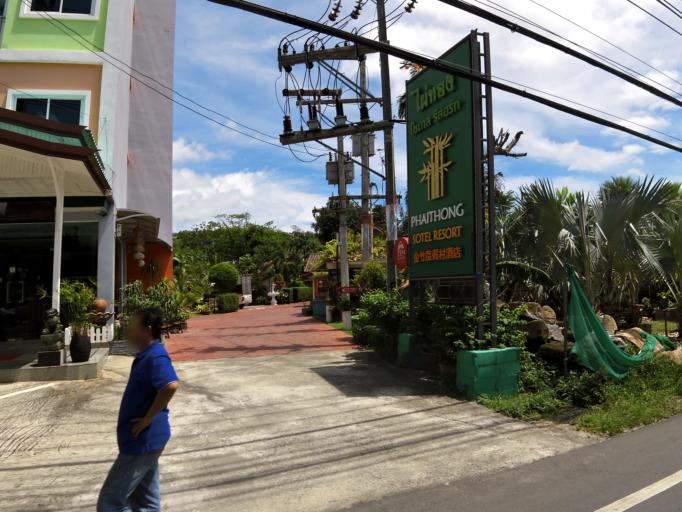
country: TH
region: Phuket
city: Ban Chalong
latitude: 7.8614
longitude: 98.3440
